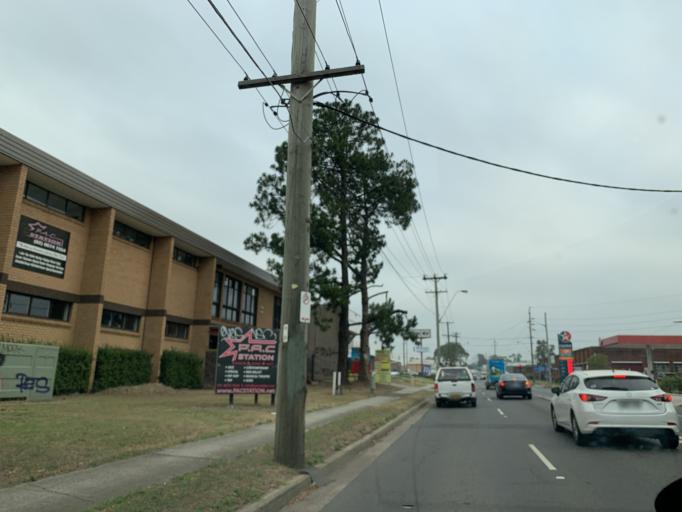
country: AU
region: New South Wales
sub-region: Holroyd
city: Girraween
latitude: -33.7749
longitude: 150.9445
